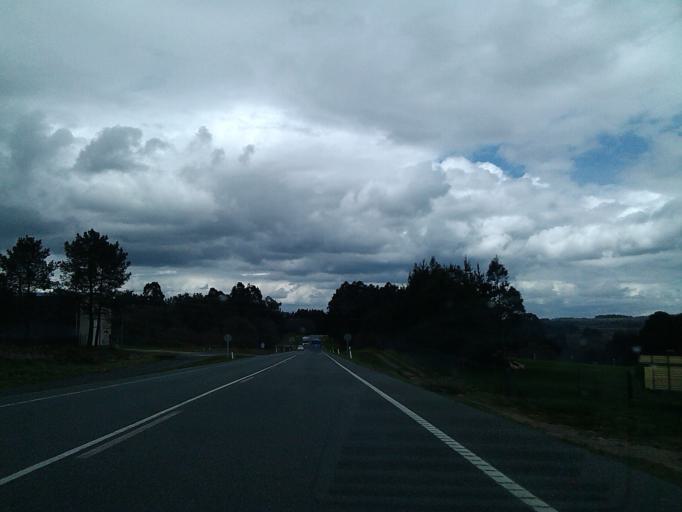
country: ES
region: Galicia
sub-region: Provincia da Coruna
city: Curtis
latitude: 43.1606
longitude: -7.9994
